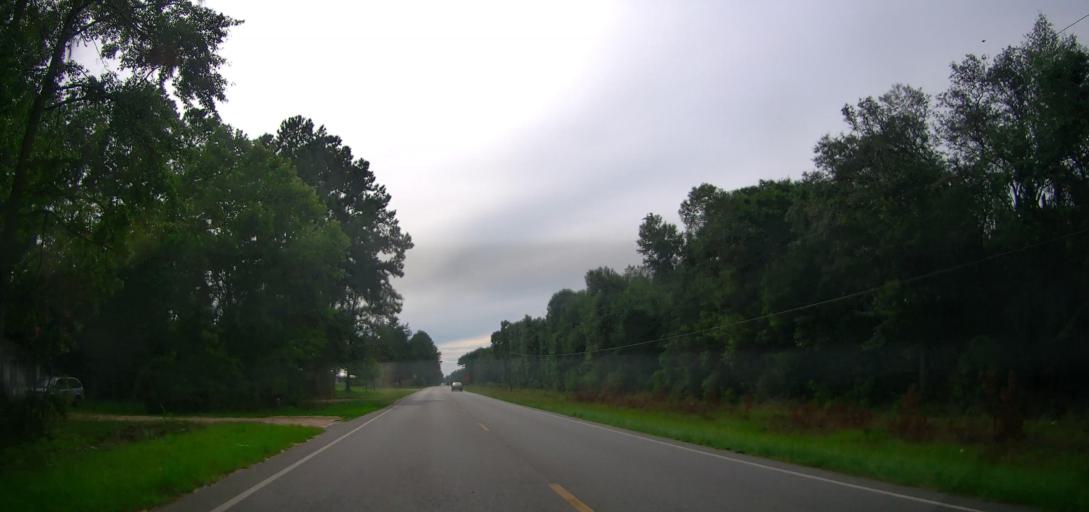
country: US
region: Georgia
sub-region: Wayne County
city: Jesup
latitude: 31.6646
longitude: -81.8638
